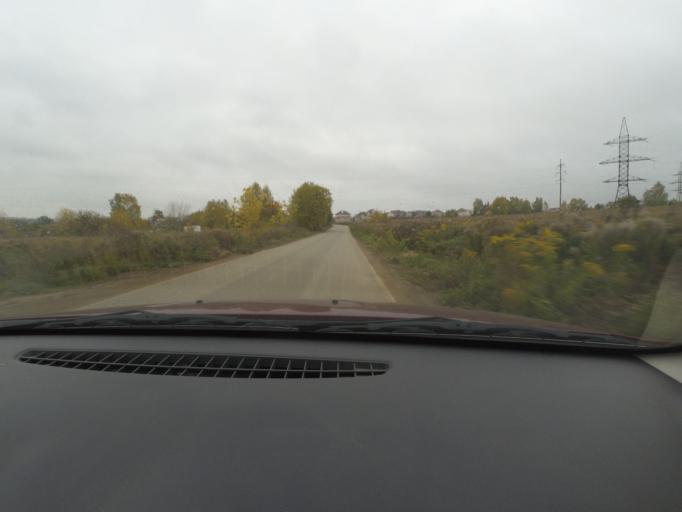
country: RU
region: Nizjnij Novgorod
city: Afonino
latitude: 56.2734
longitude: 44.0571
